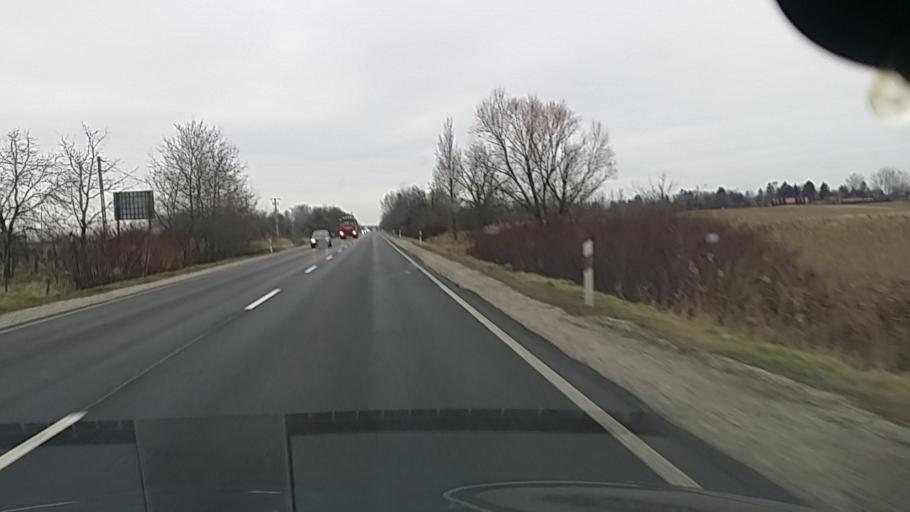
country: HU
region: Szabolcs-Szatmar-Bereg
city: Ujfeherto
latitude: 47.8697
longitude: 21.7052
